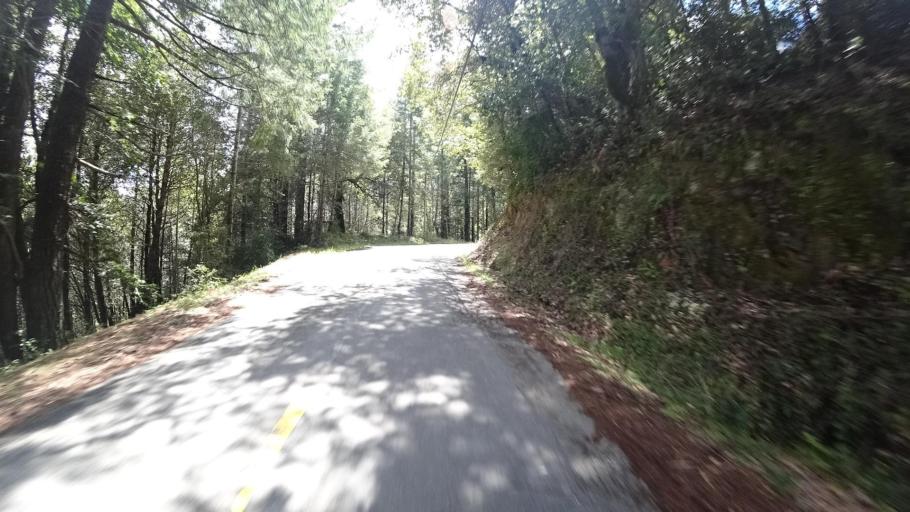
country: US
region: California
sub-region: Humboldt County
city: Blue Lake
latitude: 40.7617
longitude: -123.9593
